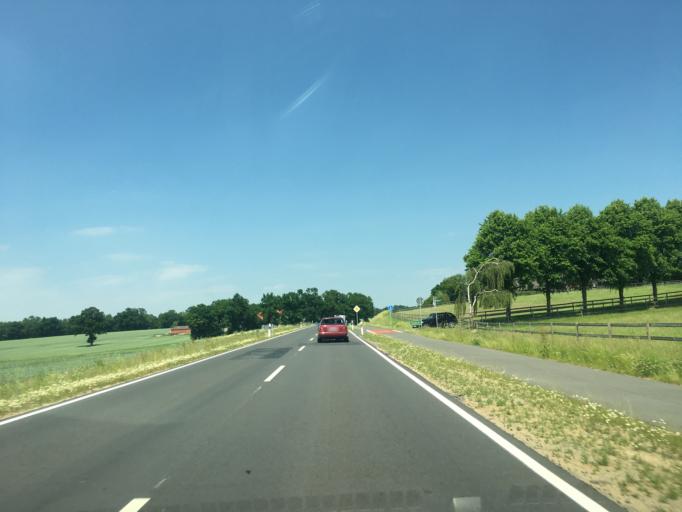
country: DE
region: North Rhine-Westphalia
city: Olfen
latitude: 51.7287
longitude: 7.4015
